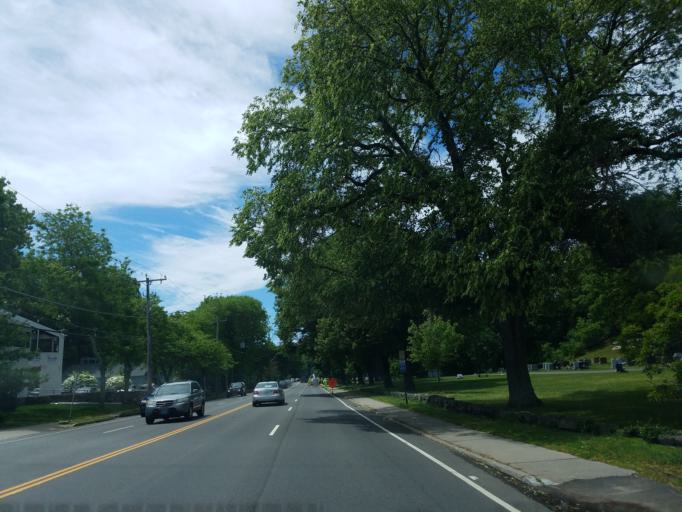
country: US
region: Connecticut
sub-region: Fairfield County
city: Darien
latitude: 41.0670
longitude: -73.4791
